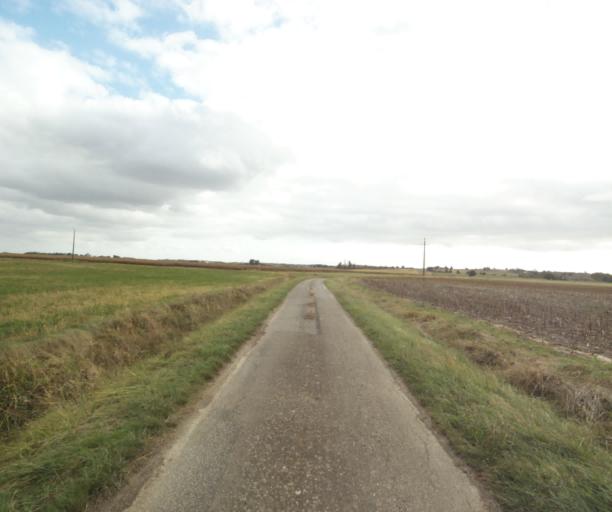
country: FR
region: Midi-Pyrenees
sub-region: Departement du Tarn-et-Garonne
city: Beaumont-de-Lomagne
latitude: 43.8886
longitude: 1.0871
